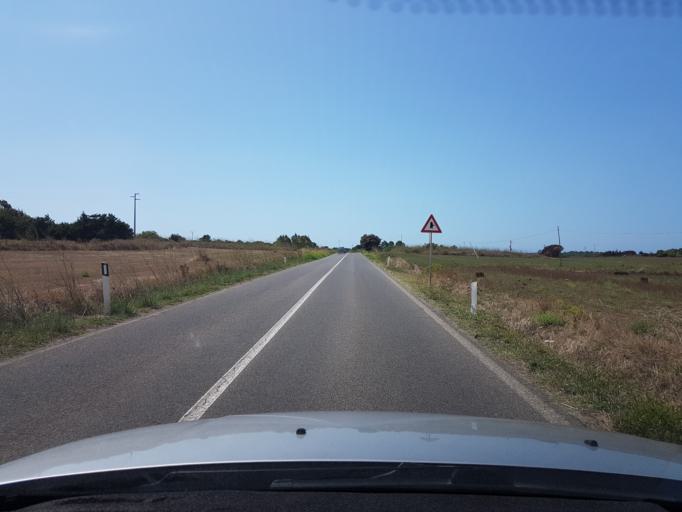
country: IT
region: Sardinia
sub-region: Provincia di Oristano
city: Riola Sardo
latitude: 40.0223
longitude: 8.4767
